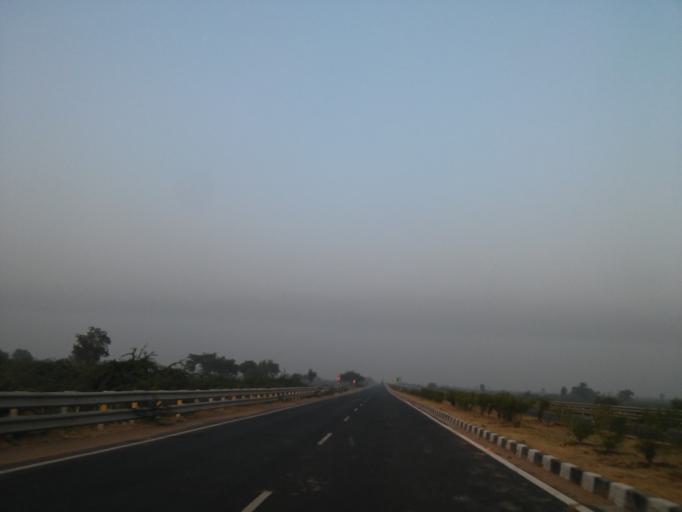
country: IN
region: Gujarat
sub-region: Surendranagar
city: Halvad
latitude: 23.0227
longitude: 70.9849
